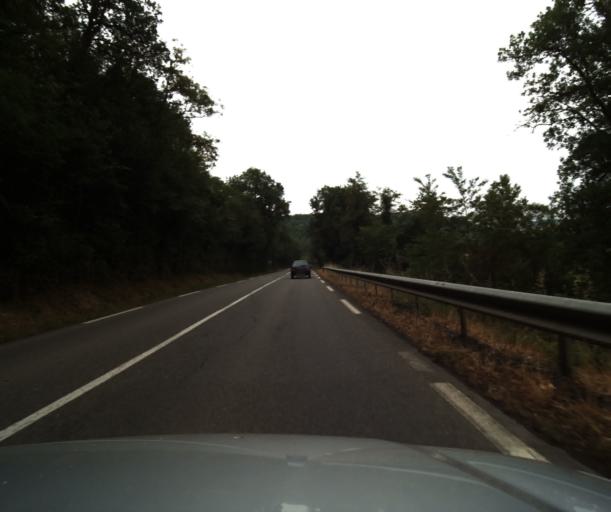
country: FR
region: Midi-Pyrenees
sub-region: Departement du Gers
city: Mielan
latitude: 43.4755
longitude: 0.3327
